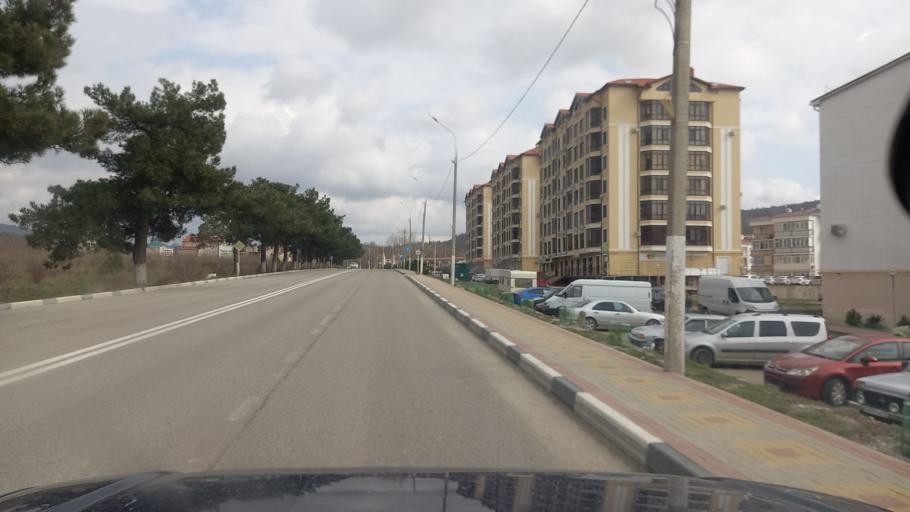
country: RU
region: Krasnodarskiy
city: Gelendzhik
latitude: 44.5557
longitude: 38.1072
